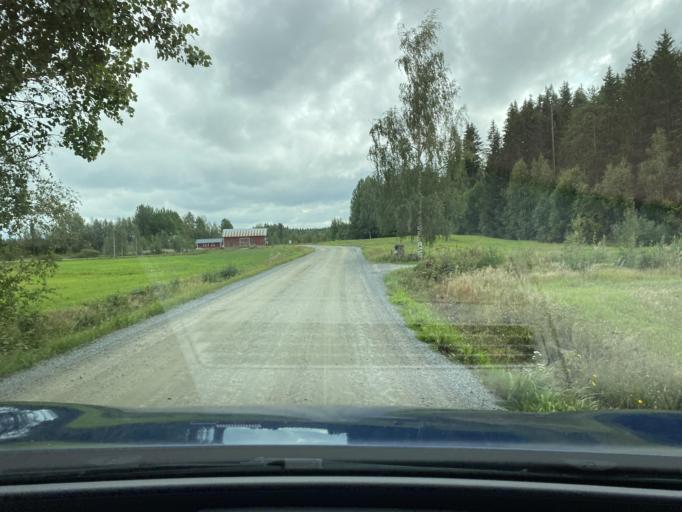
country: FI
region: Pirkanmaa
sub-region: Lounais-Pirkanmaa
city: Vammala
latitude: 61.2624
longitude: 23.0107
